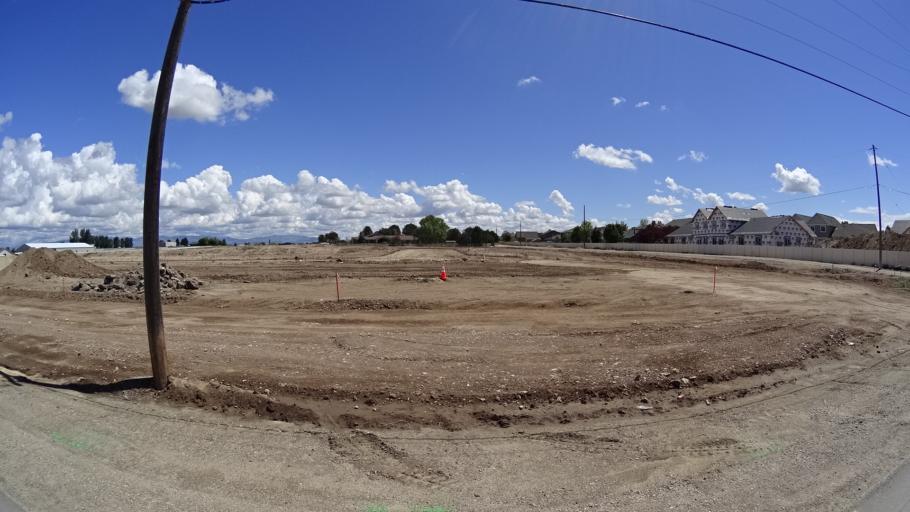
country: US
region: Idaho
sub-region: Ada County
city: Kuna
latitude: 43.5139
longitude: -116.4337
